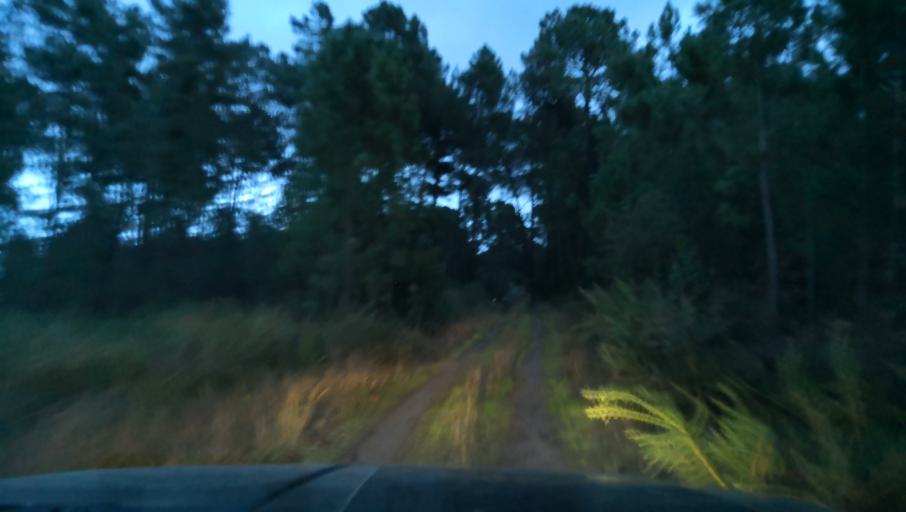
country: PT
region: Vila Real
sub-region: Vila Real
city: Vila Real
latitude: 41.2718
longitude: -7.7321
